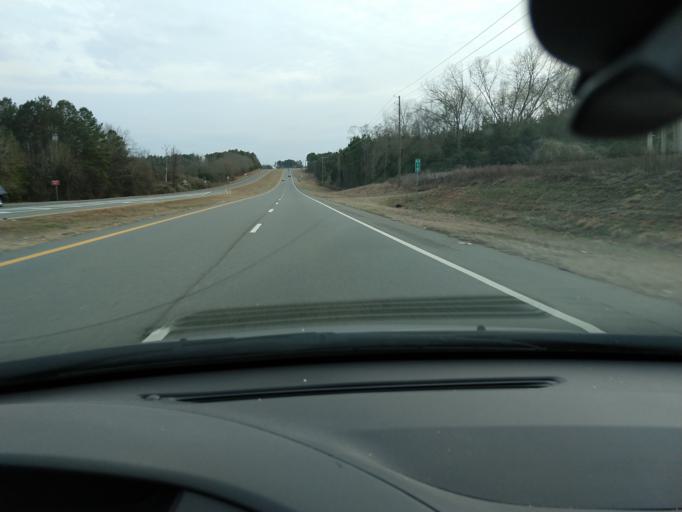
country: US
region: Georgia
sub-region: Sumter County
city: Americus
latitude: 32.0547
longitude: -84.2541
